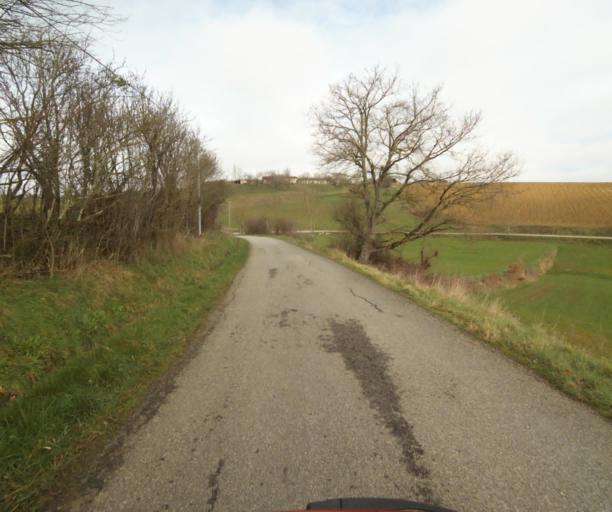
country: FR
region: Midi-Pyrenees
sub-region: Departement de l'Ariege
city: Saverdun
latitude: 43.1694
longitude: 1.5107
